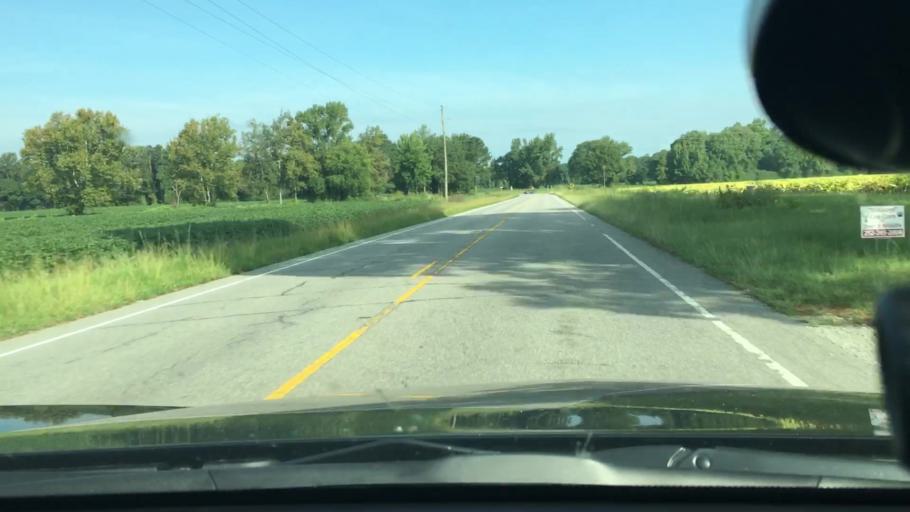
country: US
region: North Carolina
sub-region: Edgecombe County
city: Pinetops
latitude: 35.7516
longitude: -77.5454
